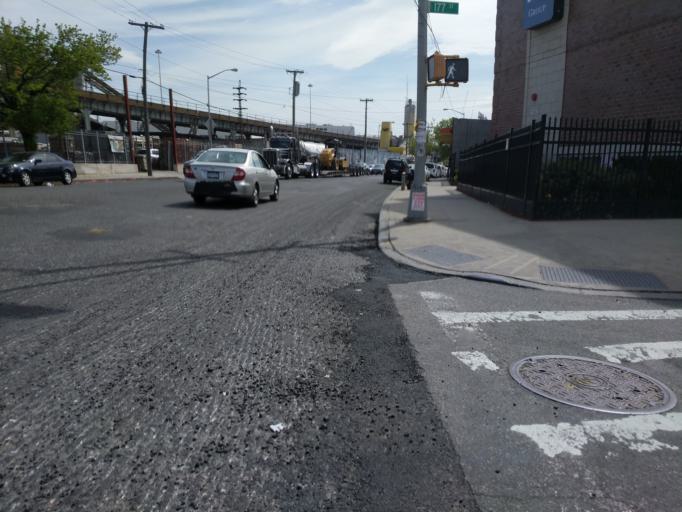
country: US
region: New York
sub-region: Queens County
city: Jamaica
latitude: 40.7053
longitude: -73.7825
